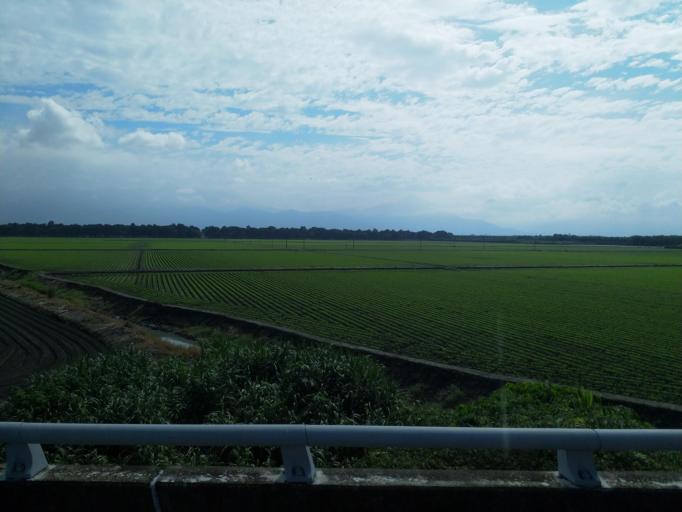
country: TW
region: Taiwan
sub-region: Pingtung
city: Pingtung
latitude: 22.8372
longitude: 120.4949
